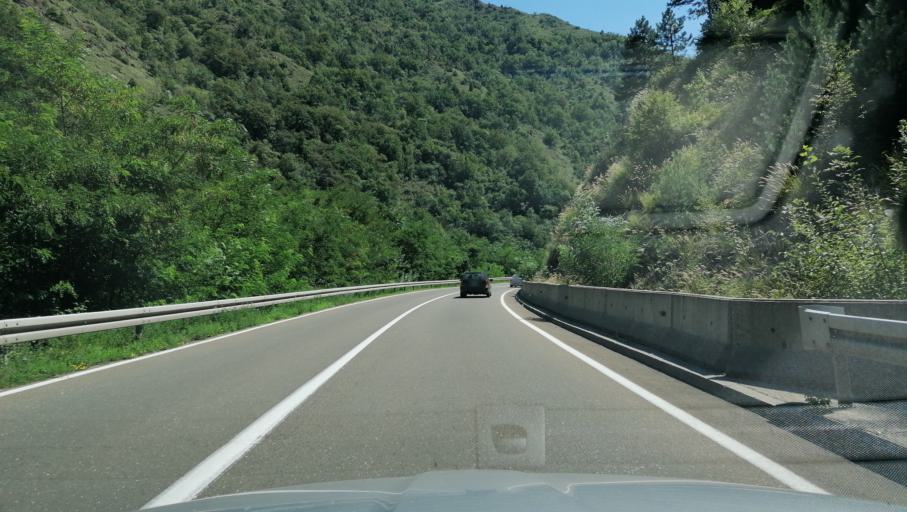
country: RS
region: Central Serbia
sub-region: Raski Okrug
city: Kraljevo
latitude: 43.5876
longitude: 20.5793
